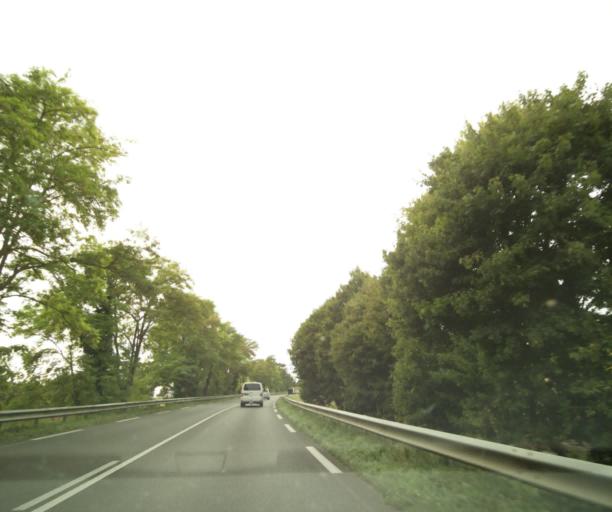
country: FR
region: Centre
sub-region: Departement d'Indre-et-Loire
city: Perrusson
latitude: 47.1086
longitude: 0.9910
